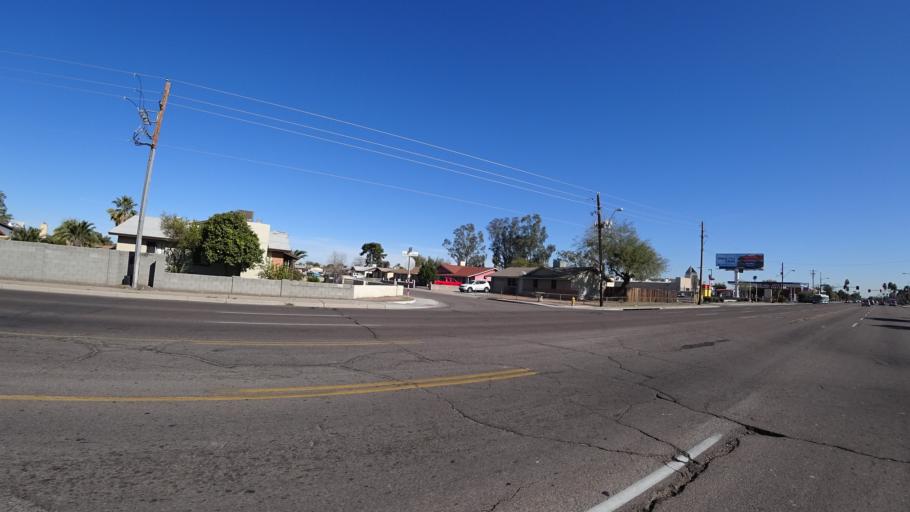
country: US
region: Arizona
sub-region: Maricopa County
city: Tolleson
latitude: 33.4942
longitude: -112.2401
